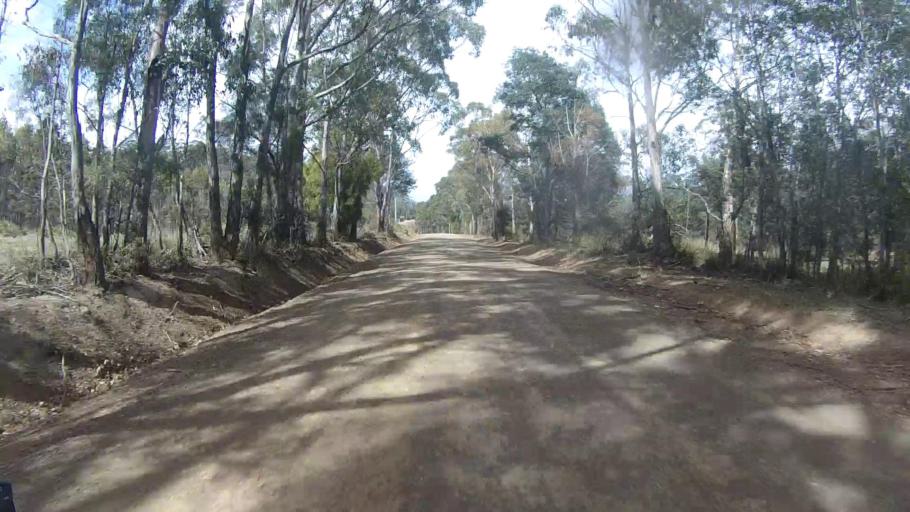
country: AU
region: Tasmania
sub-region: Sorell
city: Sorell
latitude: -42.6642
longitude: 147.8902
